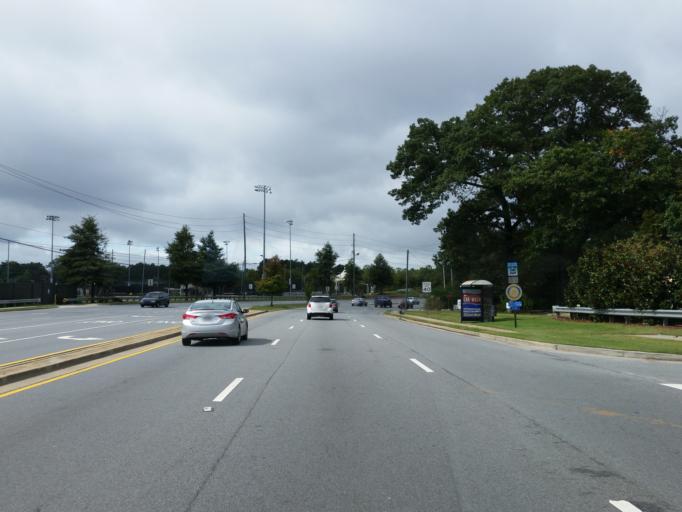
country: US
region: Georgia
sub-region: Fulton County
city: Sandy Springs
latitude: 33.9670
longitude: -84.4123
